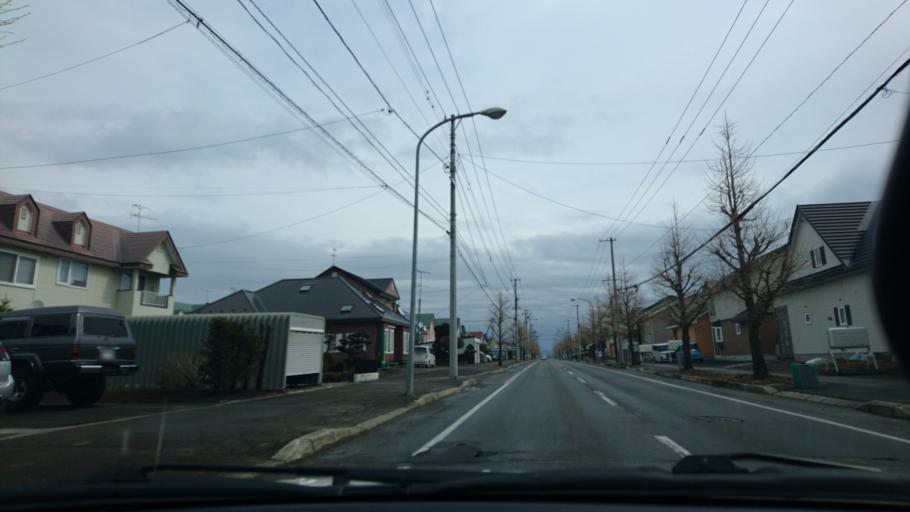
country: JP
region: Hokkaido
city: Otofuke
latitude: 42.9615
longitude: 143.1941
